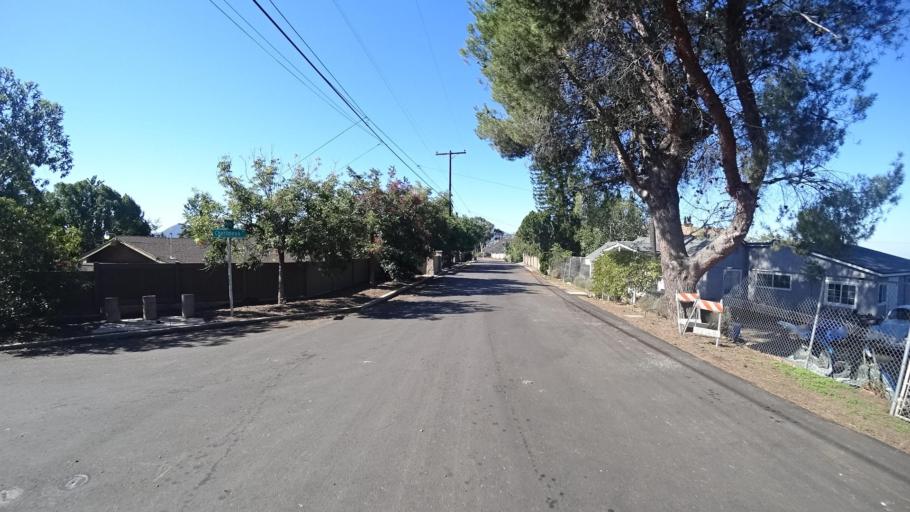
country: US
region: California
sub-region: San Diego County
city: Jamul
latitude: 32.7282
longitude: -116.8671
